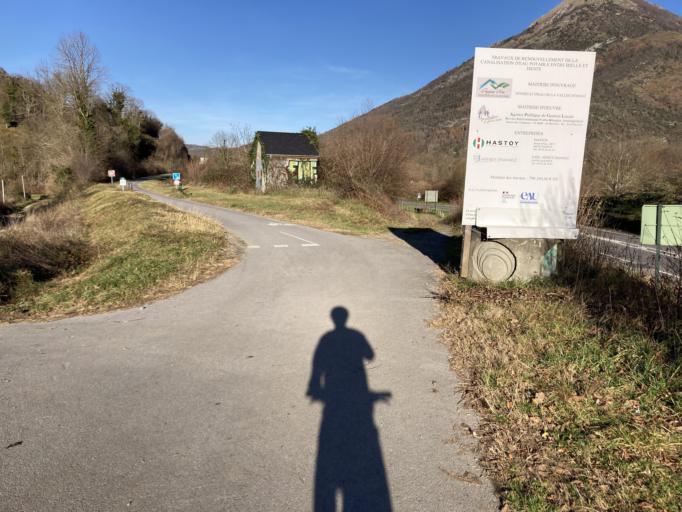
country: FR
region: Aquitaine
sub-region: Departement des Pyrenees-Atlantiques
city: Louvie-Juzon
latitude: 43.0609
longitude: -0.4266
